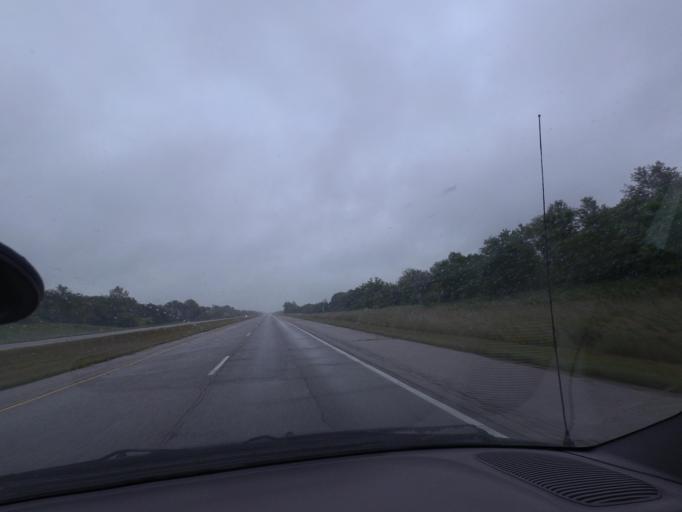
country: US
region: Illinois
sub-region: Pike County
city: Barry
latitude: 39.6913
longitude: -90.9332
